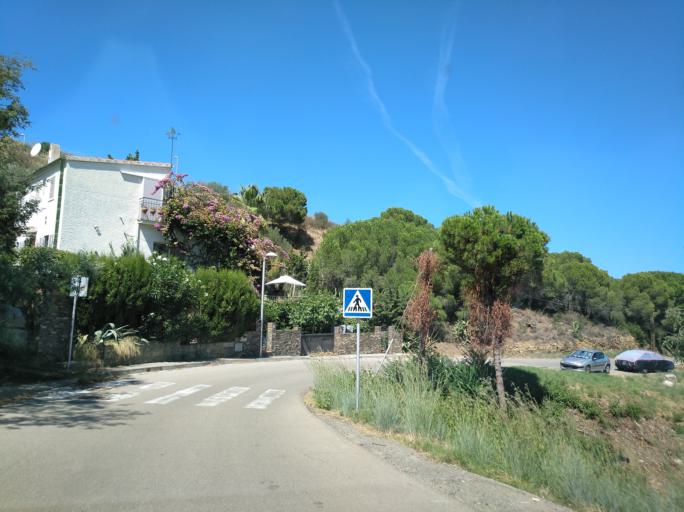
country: ES
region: Catalonia
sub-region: Provincia de Girona
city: Llanca
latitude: 42.3314
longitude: 3.1945
